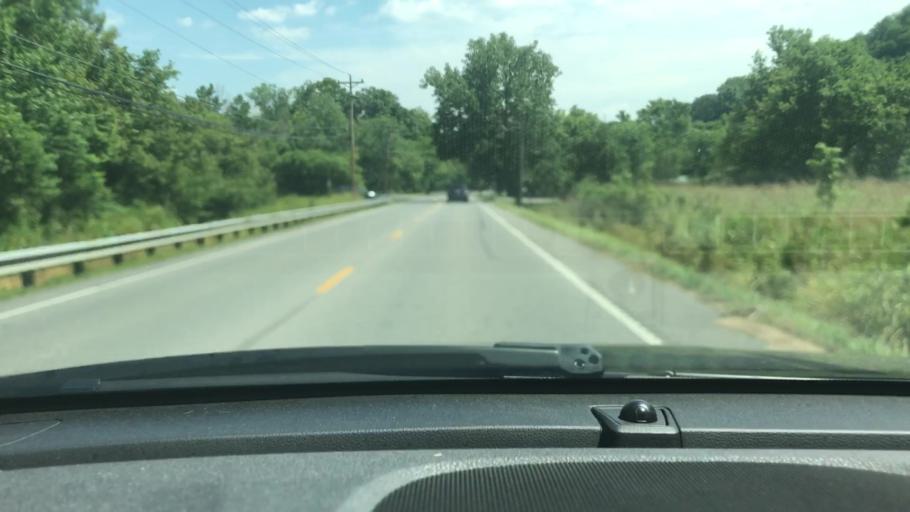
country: US
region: Tennessee
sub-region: Sumner County
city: Shackle Island
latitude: 36.3898
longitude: -86.6245
